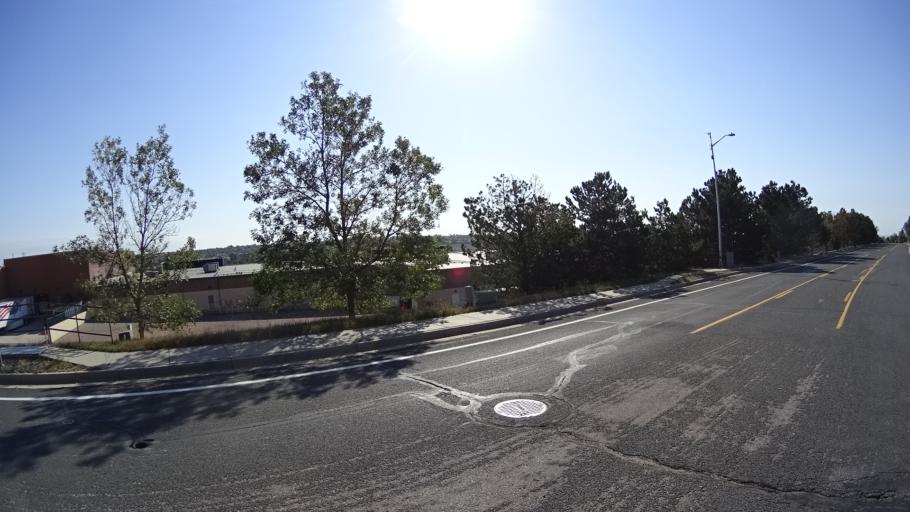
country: US
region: Colorado
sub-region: El Paso County
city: Cimarron Hills
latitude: 38.8756
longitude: -104.7233
